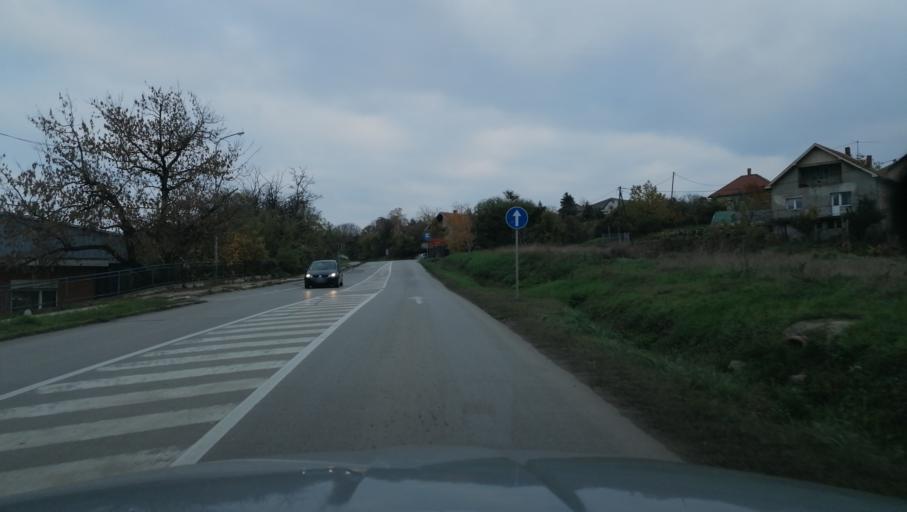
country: RS
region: Central Serbia
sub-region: Podunavski Okrug
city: Smederevo
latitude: 44.6602
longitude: 20.8936
